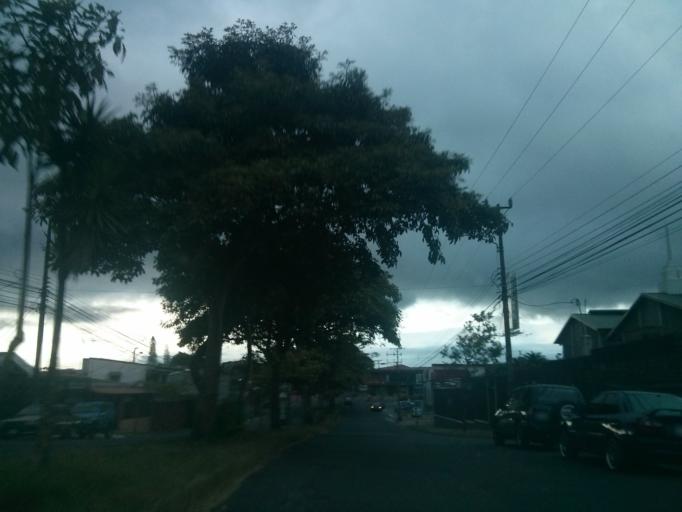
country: CR
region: San Jose
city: San Pedro
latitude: 9.9105
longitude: -84.0609
